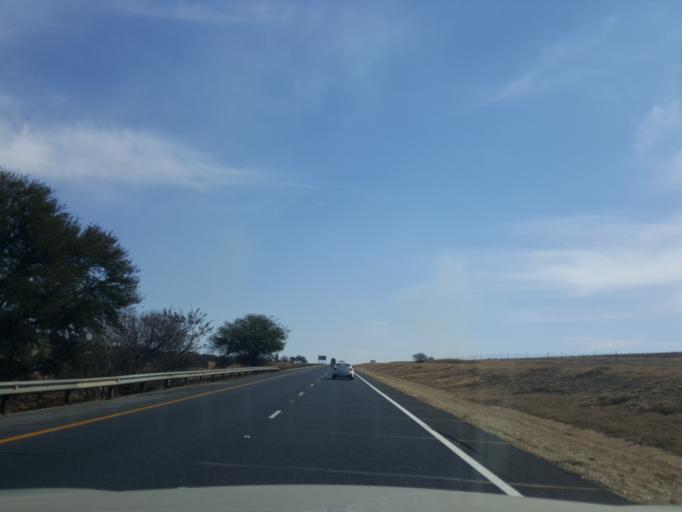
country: ZA
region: Mpumalanga
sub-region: Nkangala District Municipality
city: Witbank
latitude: -25.8787
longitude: 29.2997
